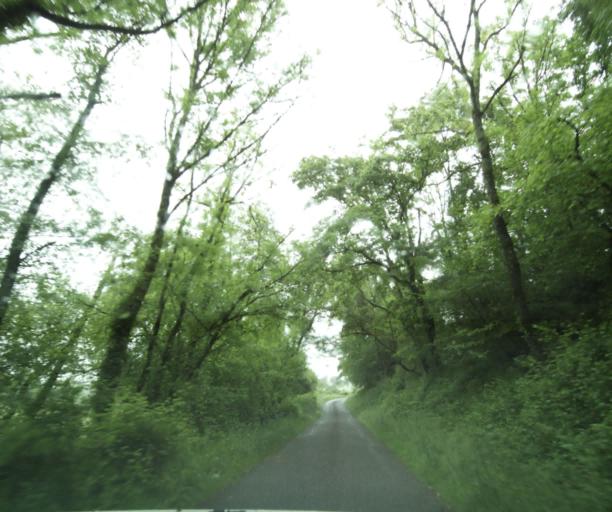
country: FR
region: Bourgogne
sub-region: Departement de Saone-et-Loire
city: Charolles
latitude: 46.3967
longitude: 4.3282
